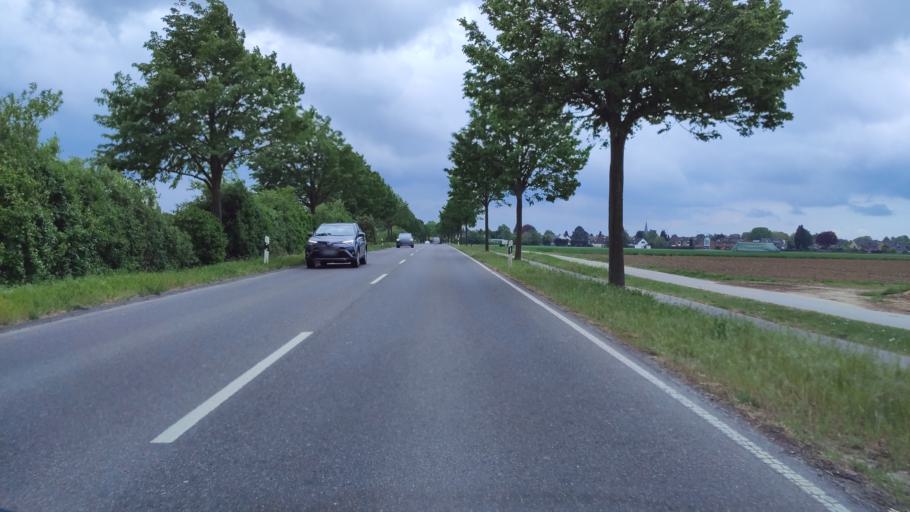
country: DE
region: North Rhine-Westphalia
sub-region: Regierungsbezirk Dusseldorf
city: Kaarst
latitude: 51.2048
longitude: 6.6188
